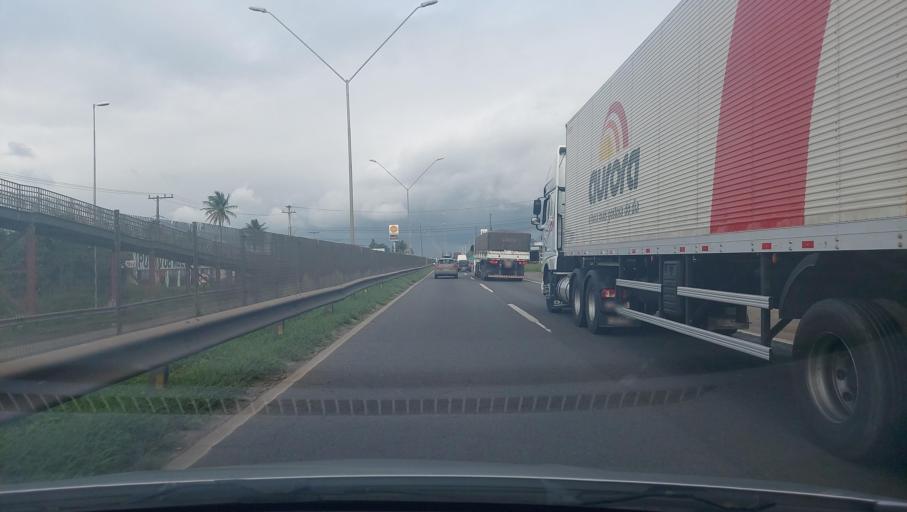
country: BR
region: Bahia
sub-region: Feira De Santana
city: Feira de Santana
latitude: -12.3136
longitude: -38.8809
